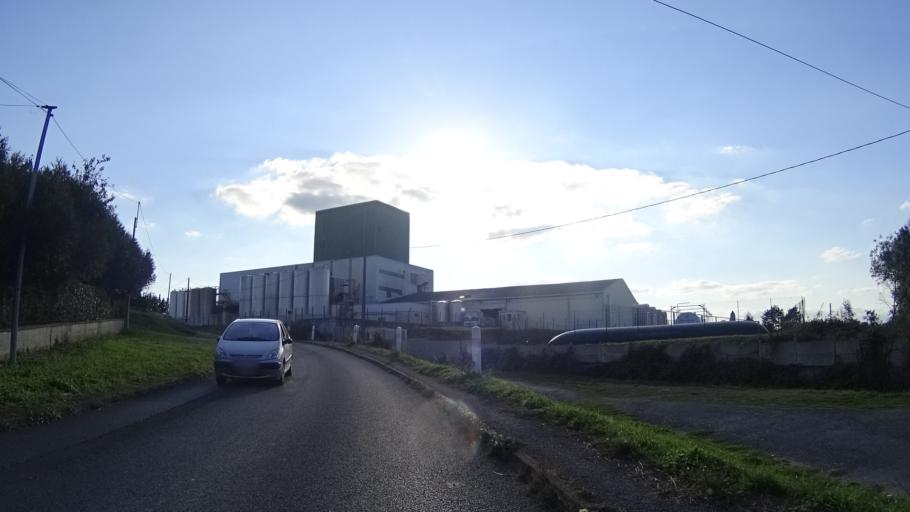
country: FR
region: Pays de la Loire
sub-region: Departement de Maine-et-Loire
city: Saint-Florent-le-Vieil
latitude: 47.3628
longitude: -1.0049
